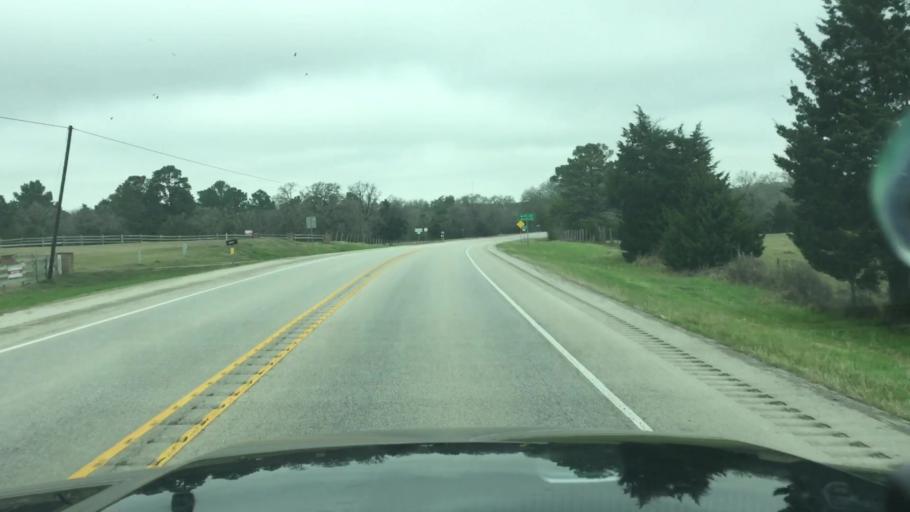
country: US
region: Texas
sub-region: Lee County
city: Giddings
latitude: 30.0805
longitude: -96.9172
